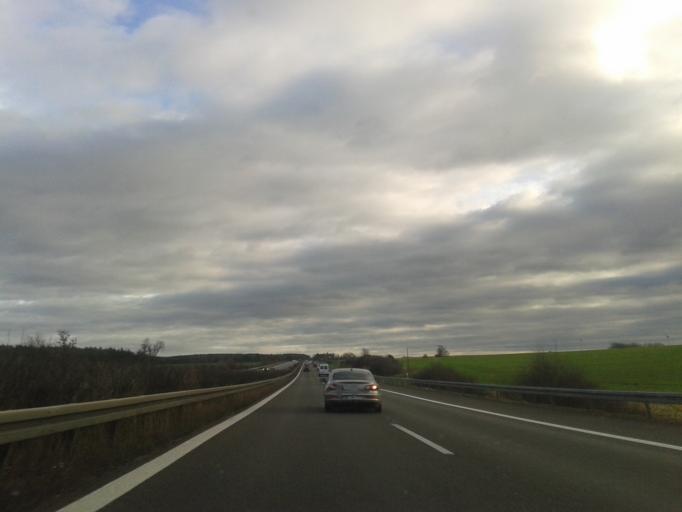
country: DE
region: Saxony
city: Wachau
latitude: 51.1712
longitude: 13.8837
